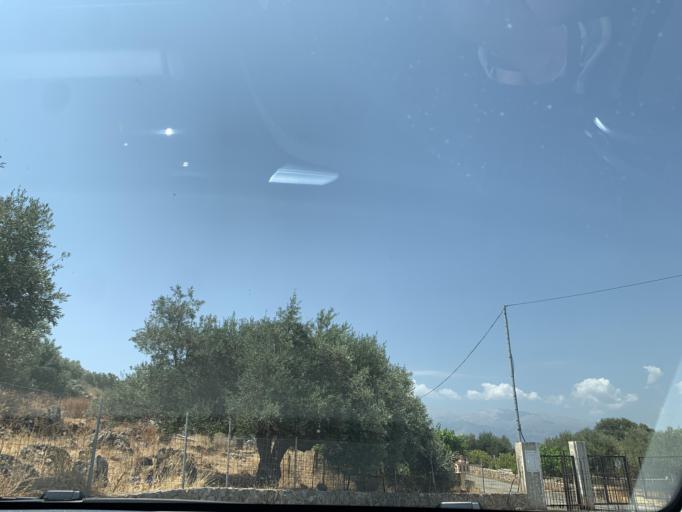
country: GR
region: Crete
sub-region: Nomos Chanias
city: Kalivai
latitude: 35.4493
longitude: 24.2275
